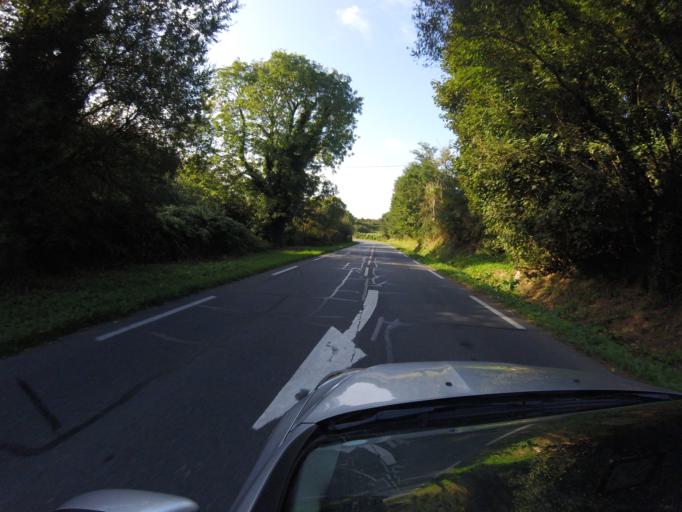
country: FR
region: Haute-Normandie
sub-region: Departement de la Seine-Maritime
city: Fecamp
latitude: 49.7672
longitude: 0.4051
